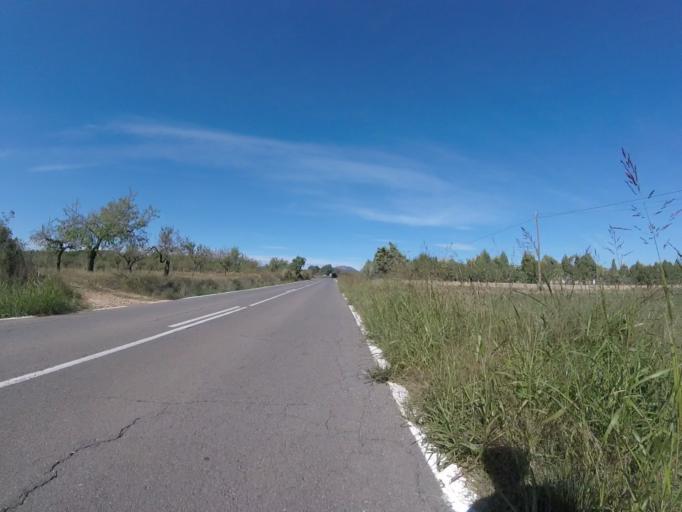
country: ES
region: Valencia
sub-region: Provincia de Castello
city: Benlloch
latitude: 40.2191
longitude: 0.0159
